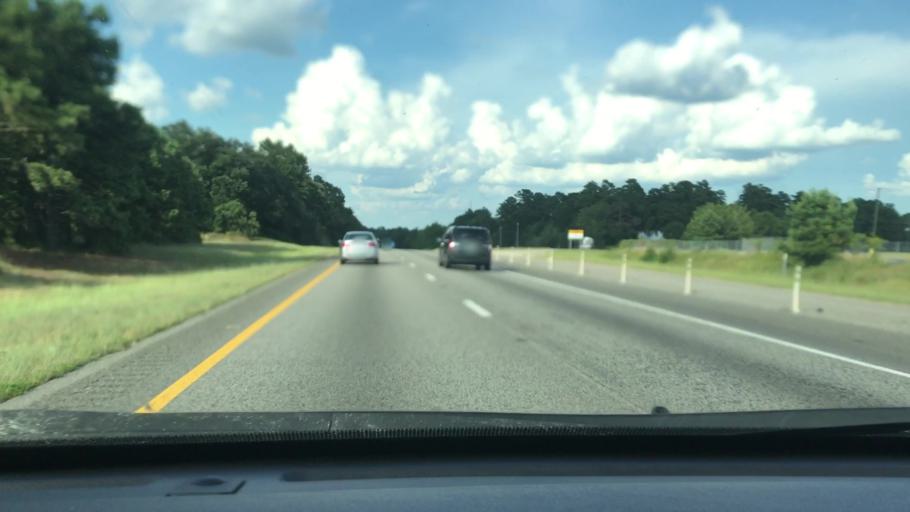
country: US
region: South Carolina
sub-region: Florence County
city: Florence
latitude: 34.2773
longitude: -79.6888
